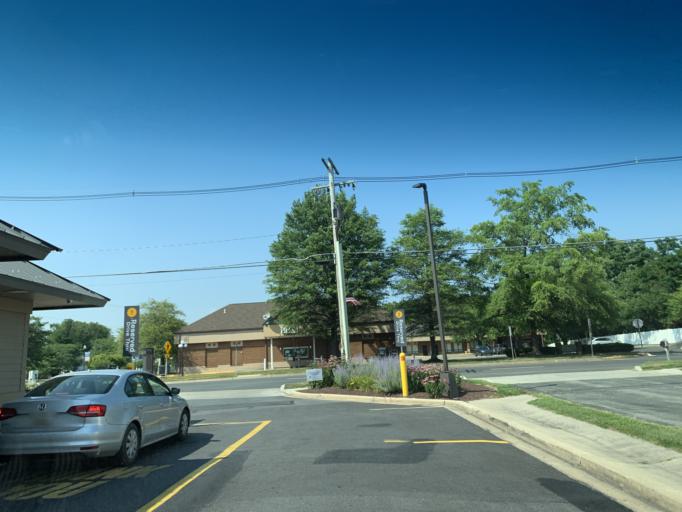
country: US
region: Maryland
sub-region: Montgomery County
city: Poolesville
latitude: 39.1441
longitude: -77.4108
